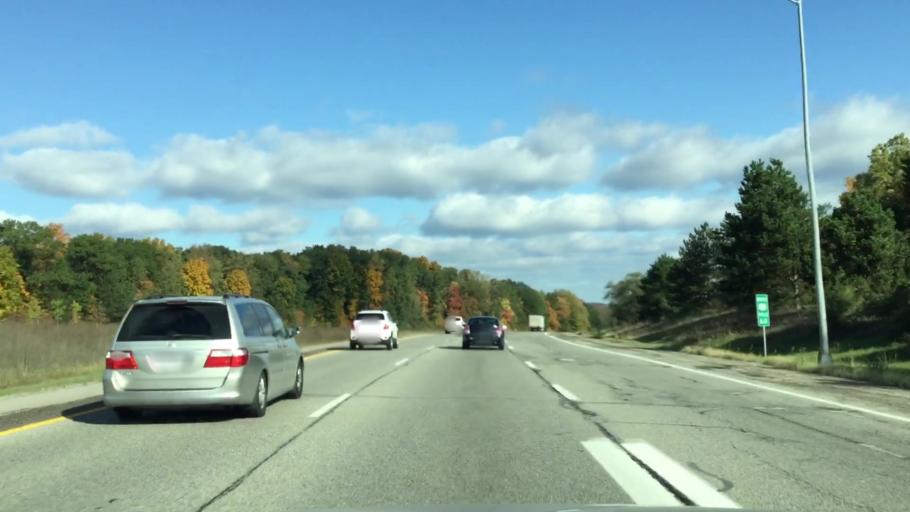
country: US
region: Michigan
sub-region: Livingston County
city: Brighton
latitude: 42.5304
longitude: -83.7520
